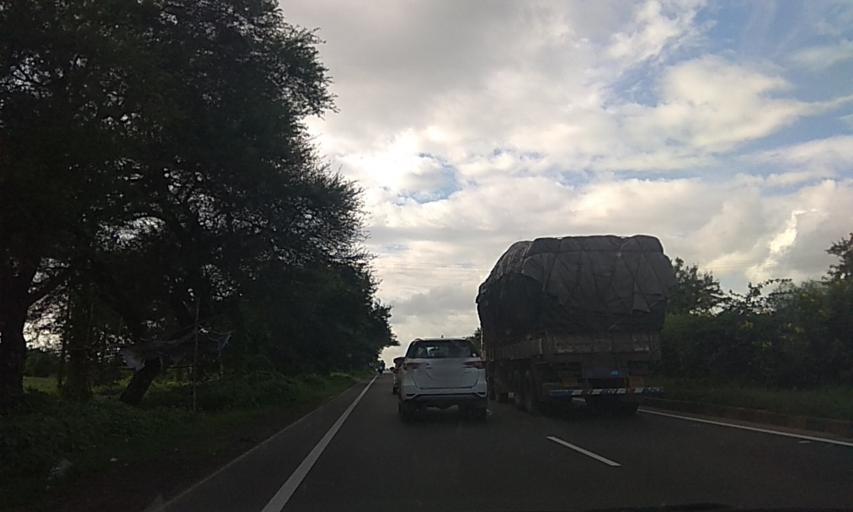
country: IN
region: Maharashtra
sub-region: Satara Division
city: Karad
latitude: 17.1130
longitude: 74.1999
